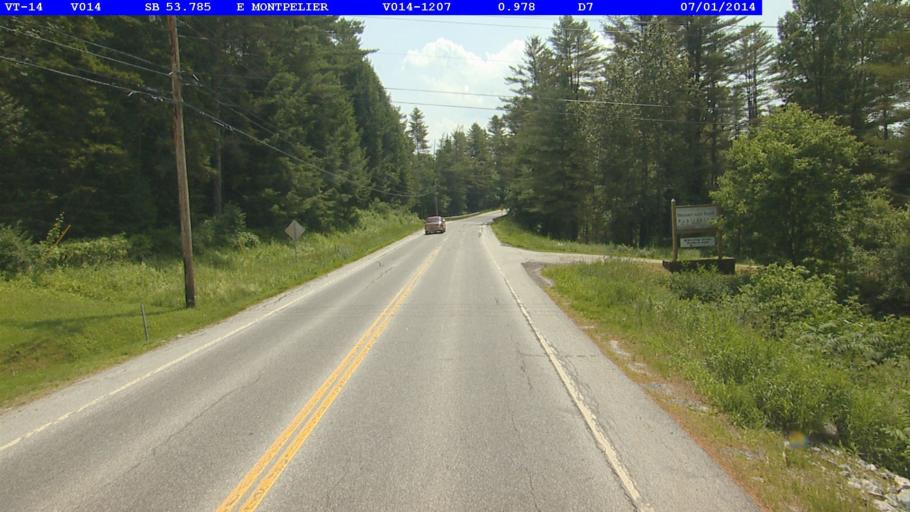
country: US
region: Vermont
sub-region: Washington County
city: Barre
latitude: 44.2490
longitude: -72.4867
